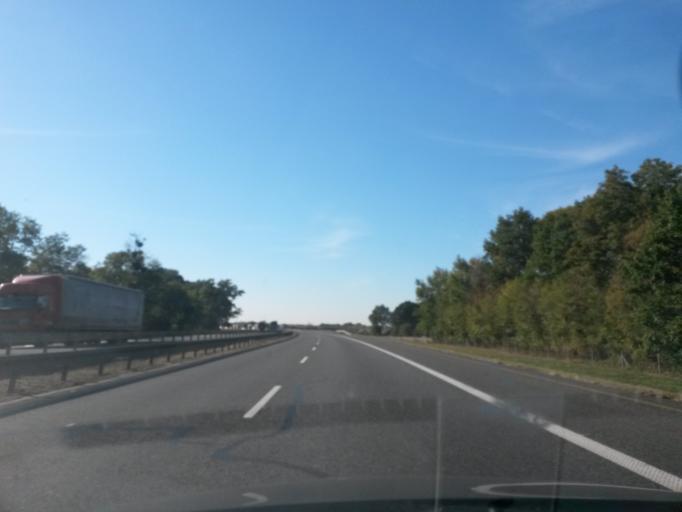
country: PL
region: Opole Voivodeship
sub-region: Powiat brzeski
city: Grodkow
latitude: 50.7684
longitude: 17.4043
